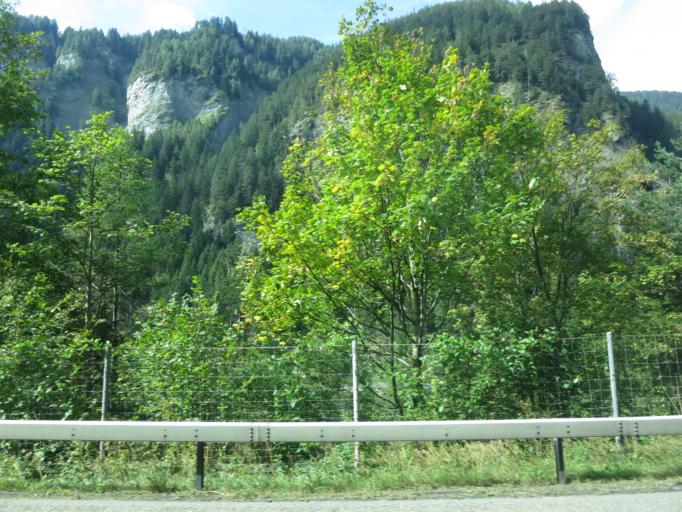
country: CH
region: Grisons
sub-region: Hinterrhein District
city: Thusis
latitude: 46.6530
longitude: 9.4514
